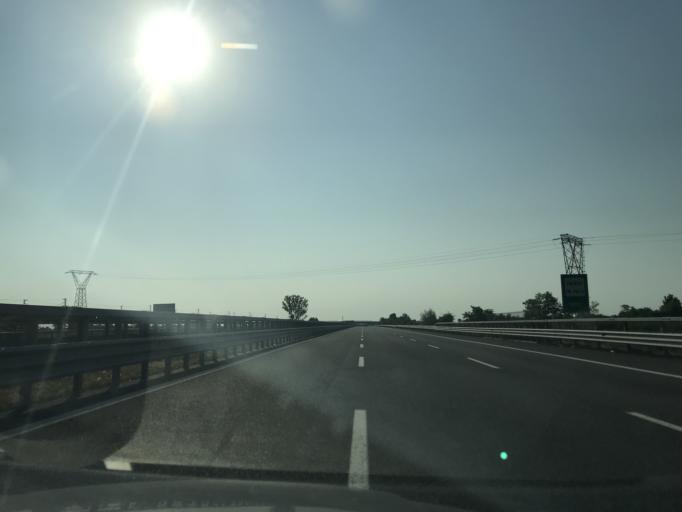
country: IT
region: Lombardy
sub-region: Provincia di Bergamo
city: Casirate d'Adda
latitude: 45.5060
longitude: 9.5660
